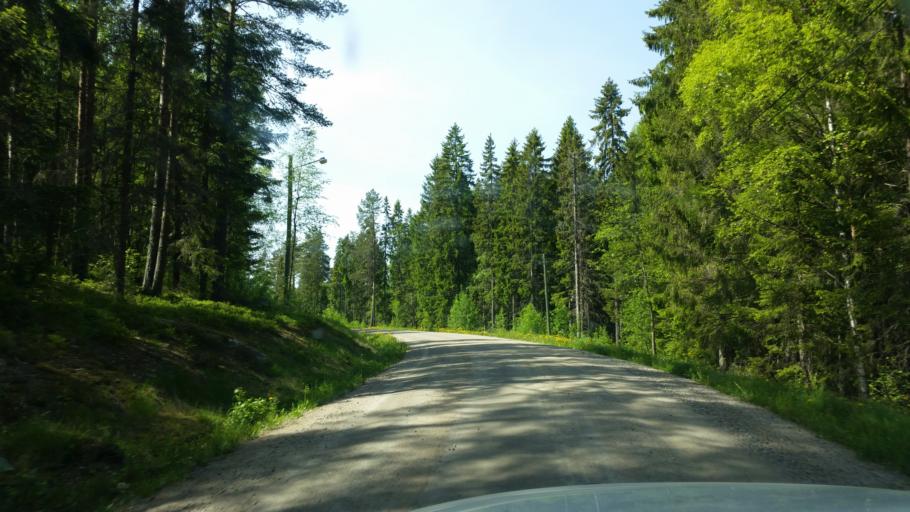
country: SE
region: Gaevleborg
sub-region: Hudiksvalls Kommun
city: Hudiksvall
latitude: 61.8125
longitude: 17.1374
